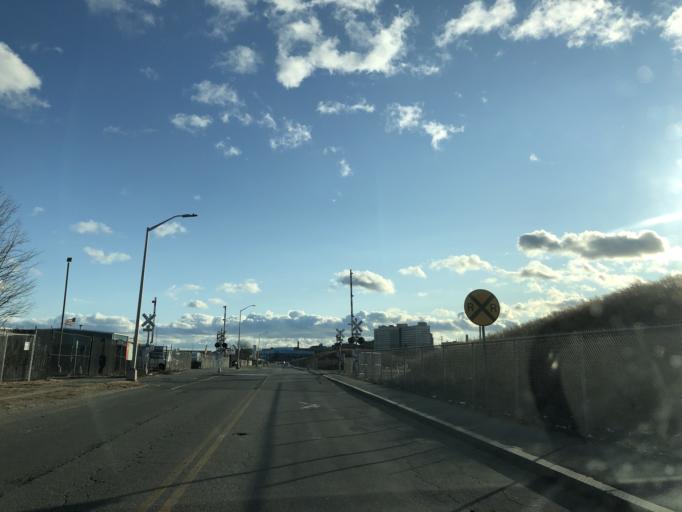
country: US
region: Massachusetts
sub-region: Bristol County
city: New Bedford
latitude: 41.6463
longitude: -70.9240
